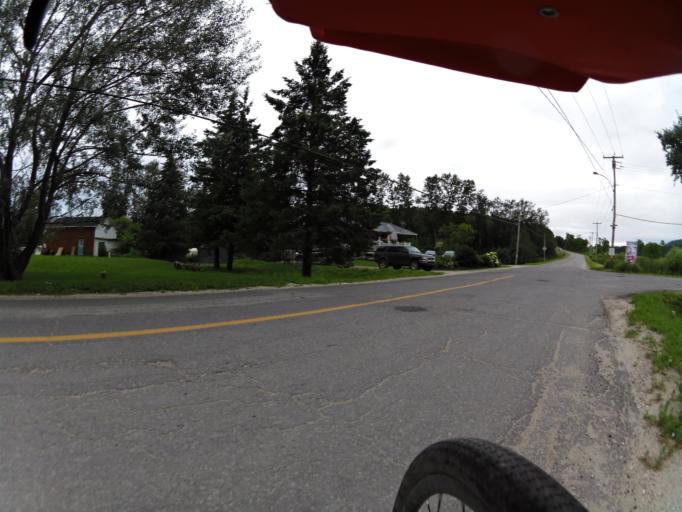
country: CA
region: Quebec
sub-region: Outaouais
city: Wakefield
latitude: 45.7085
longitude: -75.9610
